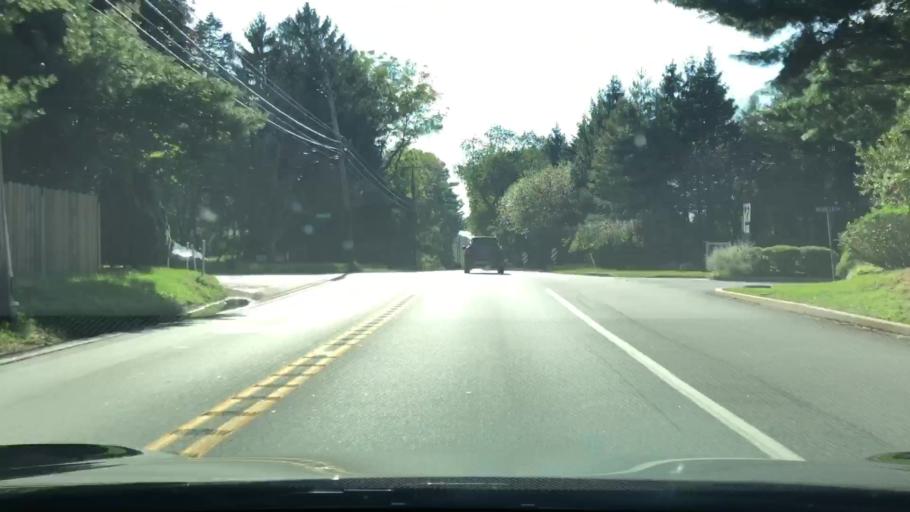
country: US
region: Pennsylvania
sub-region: Delaware County
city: Chester Heights
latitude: 39.9483
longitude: -75.5150
